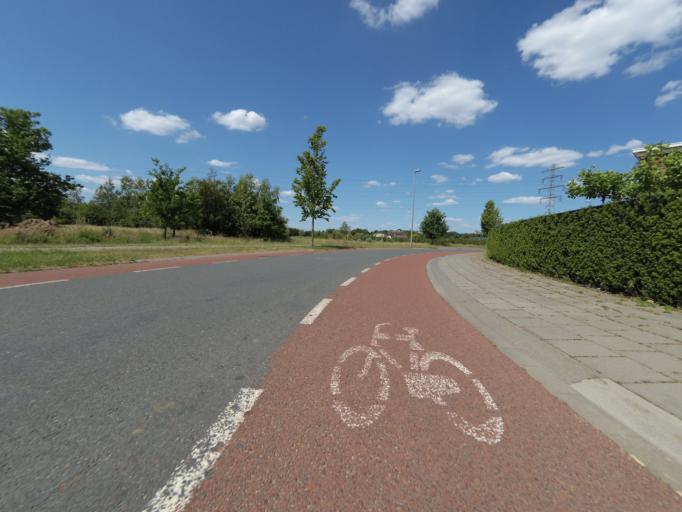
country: NL
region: Gelderland
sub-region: Gemeente Barneveld
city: Kootwijkerbroek
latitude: 52.1495
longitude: 5.6554
